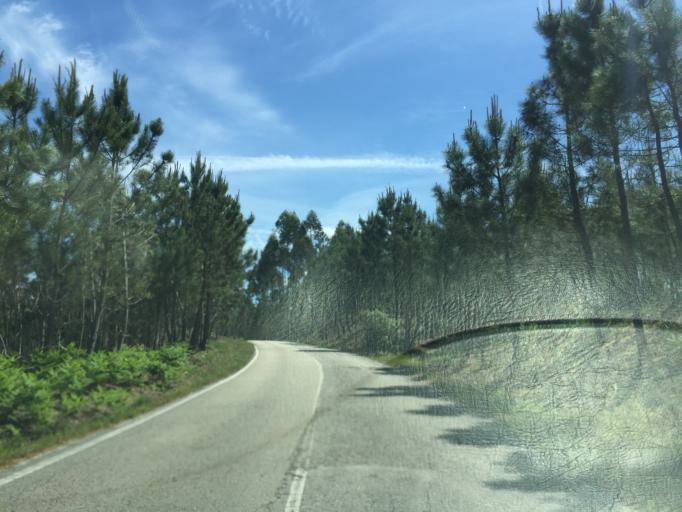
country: PT
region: Leiria
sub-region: Pombal
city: Lourical
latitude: 40.0632
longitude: -8.7095
